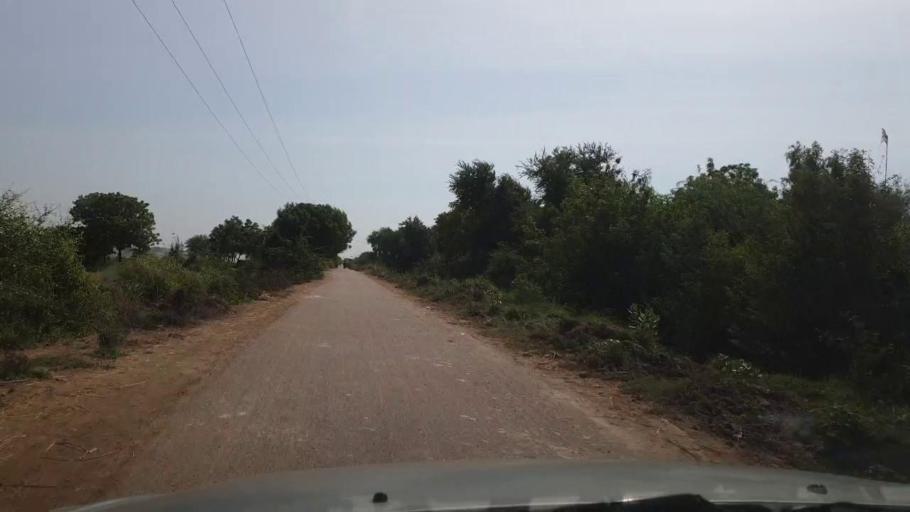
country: PK
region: Sindh
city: Tando Muhammad Khan
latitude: 25.1500
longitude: 68.3905
